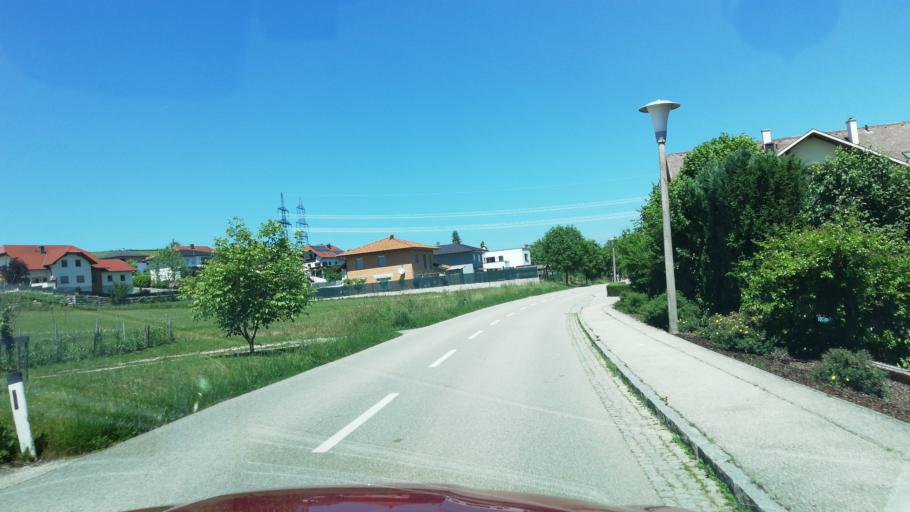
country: AT
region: Upper Austria
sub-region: Wels-Land
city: Bachmanning
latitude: 48.1334
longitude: 13.7965
